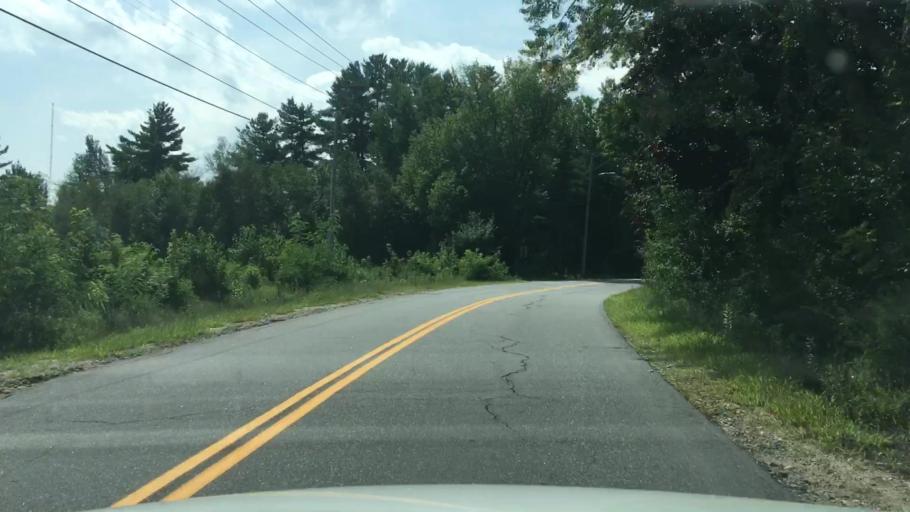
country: US
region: Maine
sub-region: Oxford County
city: Rumford
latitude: 44.5186
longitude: -70.5159
